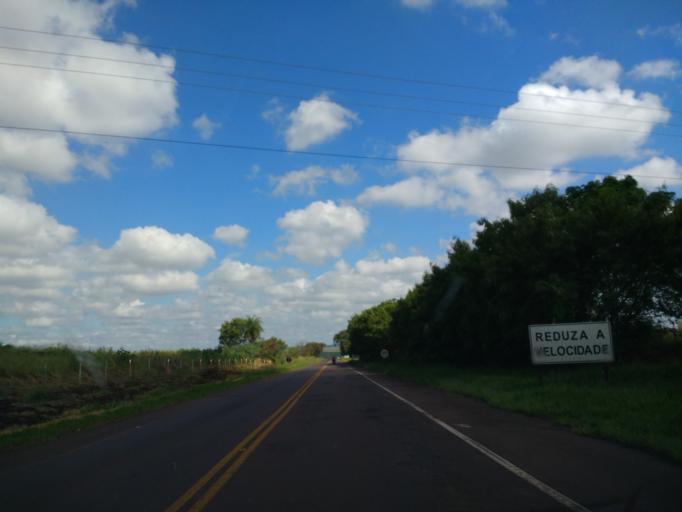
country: BR
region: Parana
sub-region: Alto Piquiri
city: Alto Piquiri
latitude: -23.9032
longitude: -53.4739
